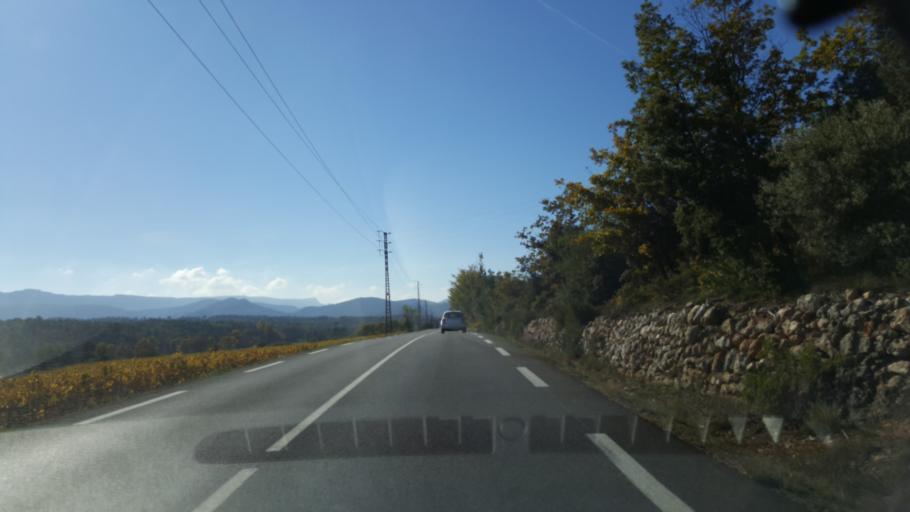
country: FR
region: Provence-Alpes-Cote d'Azur
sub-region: Departement du Var
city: Rougiers
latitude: 43.4034
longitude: 5.8140
